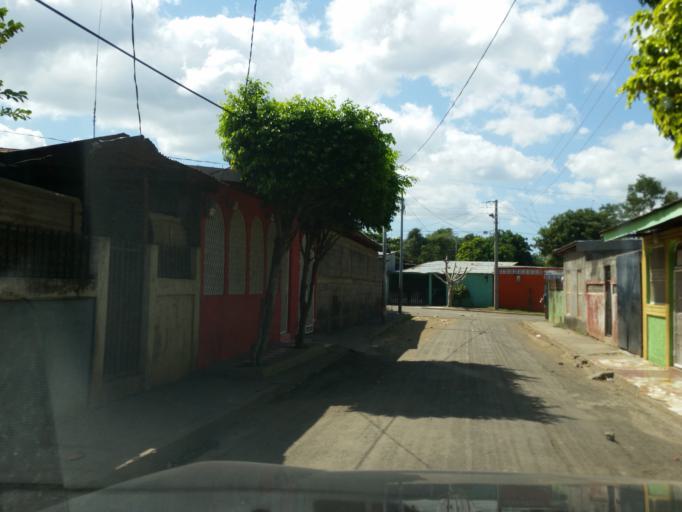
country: NI
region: Managua
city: Managua
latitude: 12.1168
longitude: -86.2393
